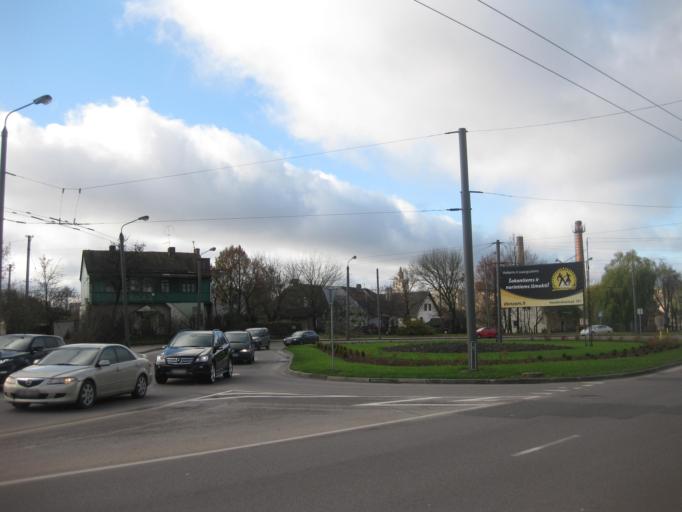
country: LT
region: Kauno apskritis
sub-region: Kaunas
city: Kaunas
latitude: 54.9056
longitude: 23.8841
